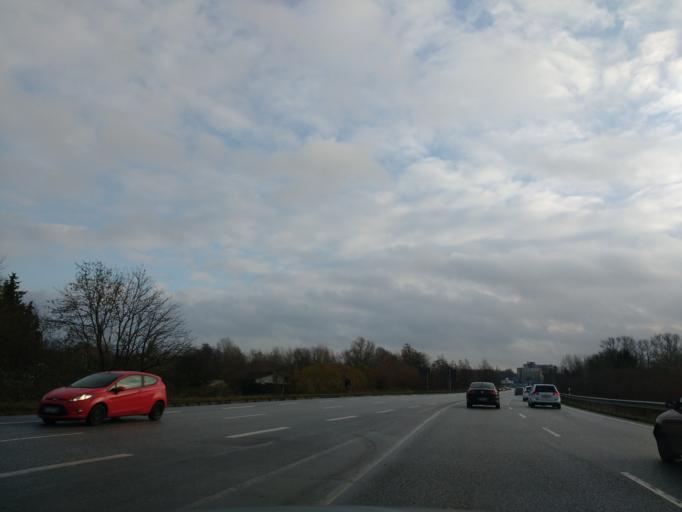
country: DE
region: Schleswig-Holstein
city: Eckernforde
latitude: 54.4690
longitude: 9.8298
